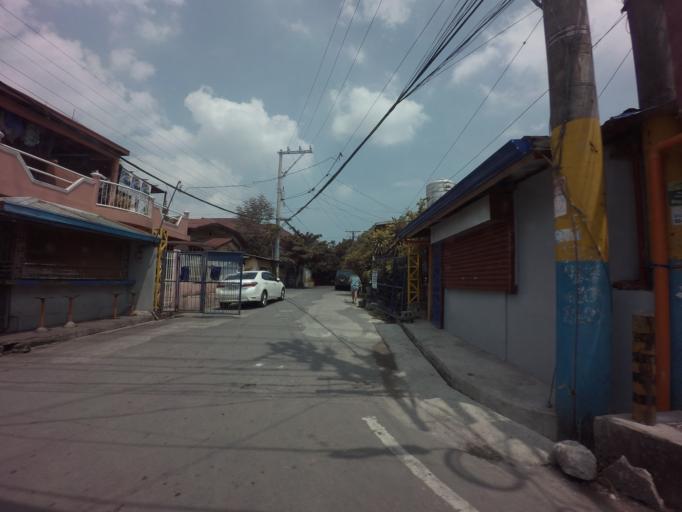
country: PH
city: Sambayanihan People's Village
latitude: 14.4567
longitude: 121.0530
